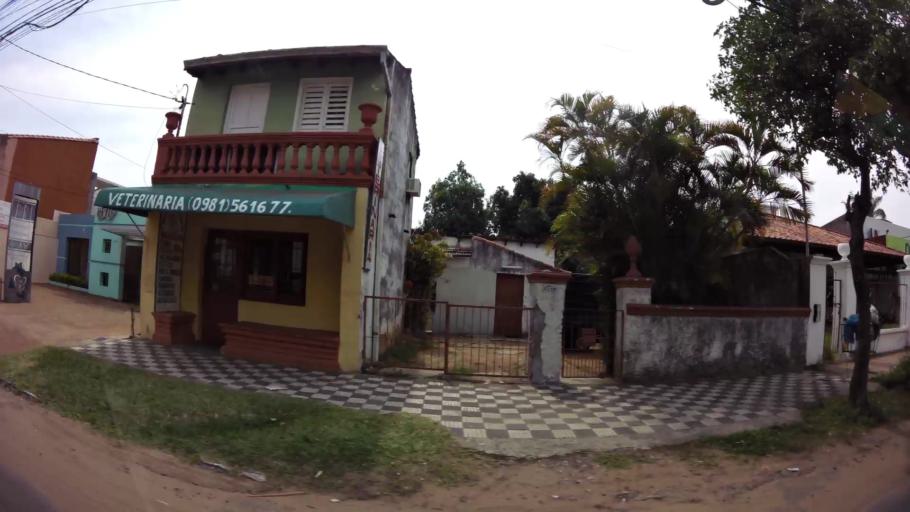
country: PY
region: Asuncion
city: Asuncion
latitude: -25.2716
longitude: -57.5649
